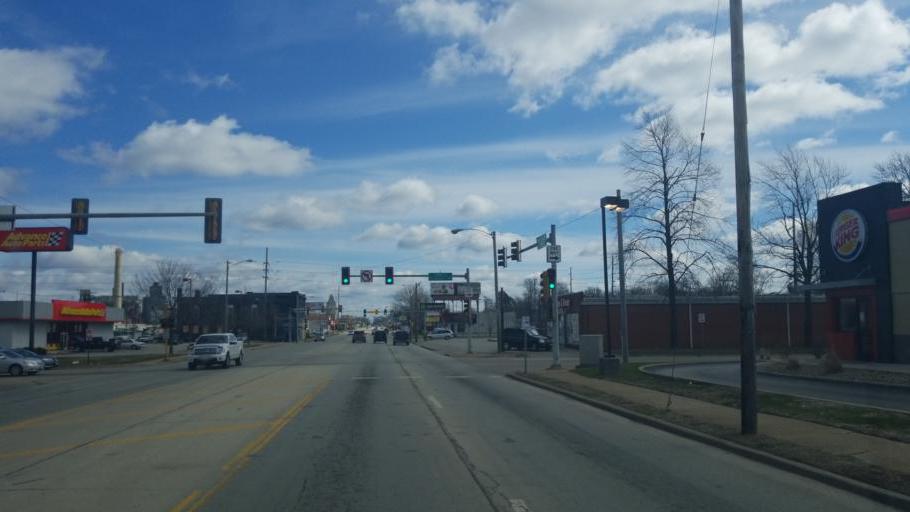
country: US
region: Illinois
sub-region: Macon County
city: Decatur
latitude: 39.8461
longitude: -88.9423
